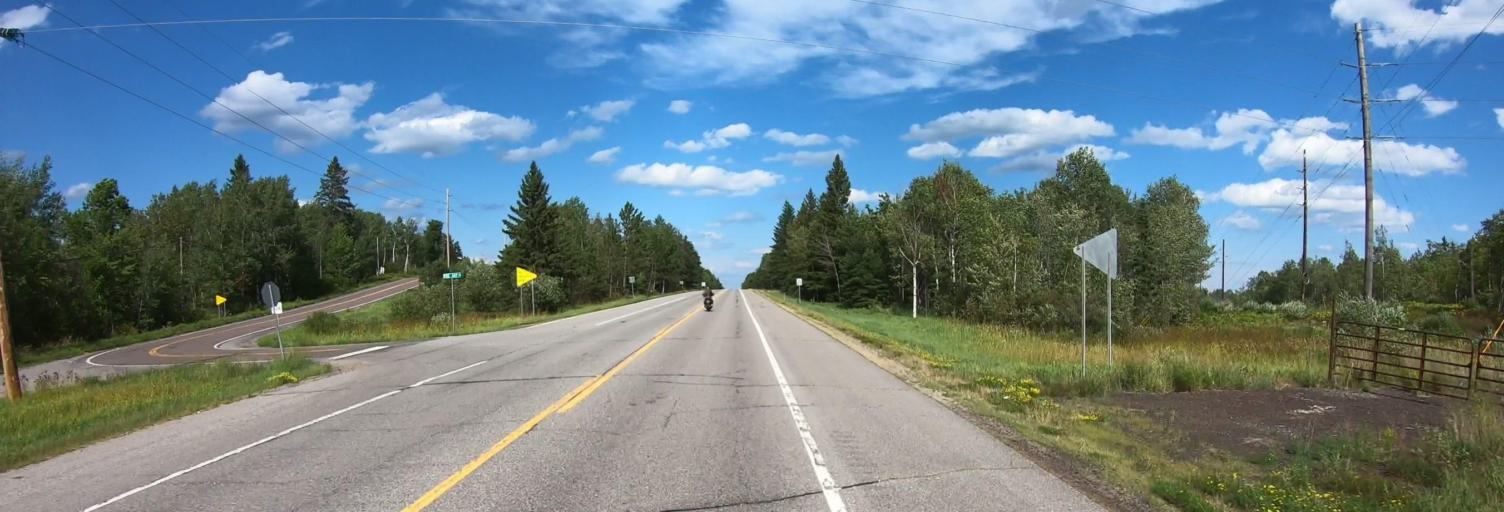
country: US
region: Minnesota
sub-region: Saint Louis County
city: Aurora
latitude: 47.7872
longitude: -92.3588
